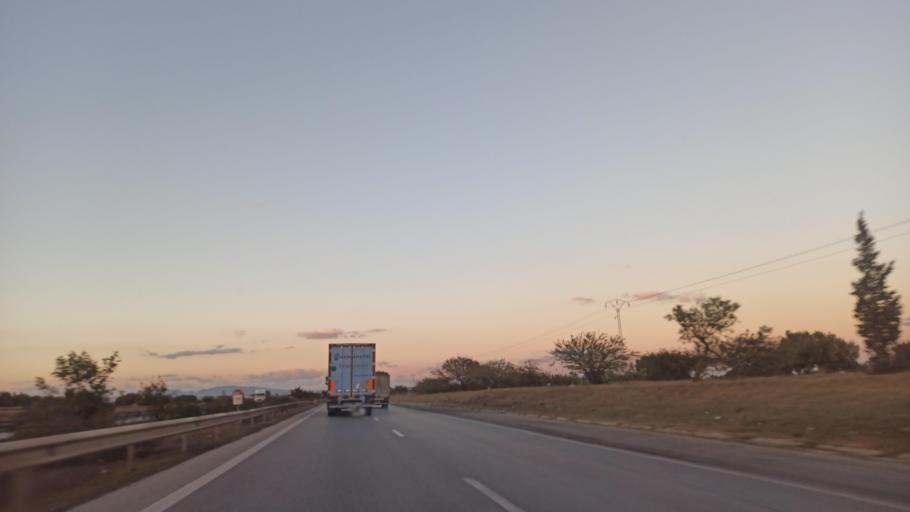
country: TN
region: Nabul
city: Al Hammamat
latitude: 36.2685
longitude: 10.4319
